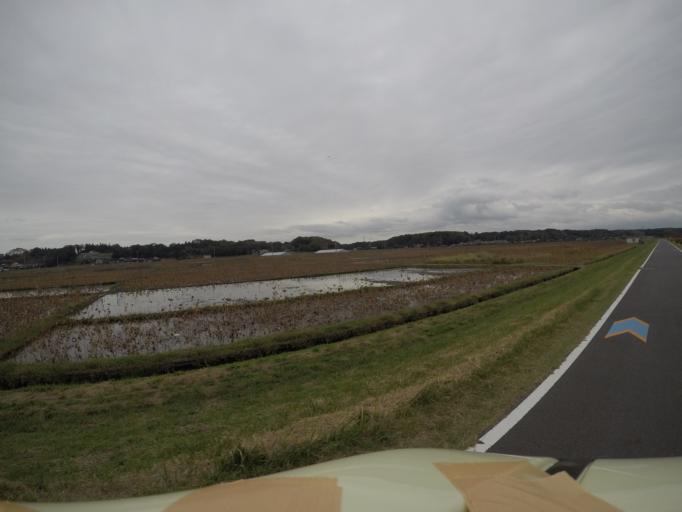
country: JP
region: Ibaraki
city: Ami
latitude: 36.0678
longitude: 140.2701
